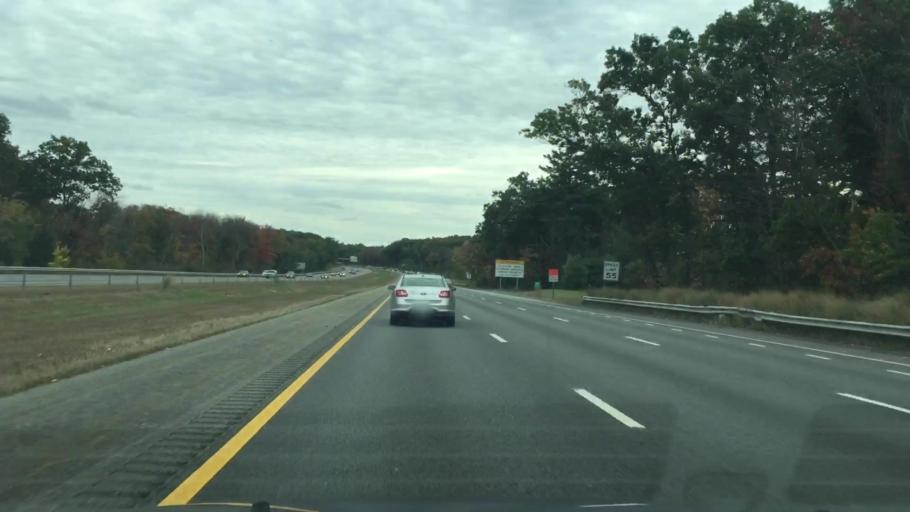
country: US
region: Massachusetts
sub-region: Middlesex County
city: Billerica
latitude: 42.5393
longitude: -71.2814
